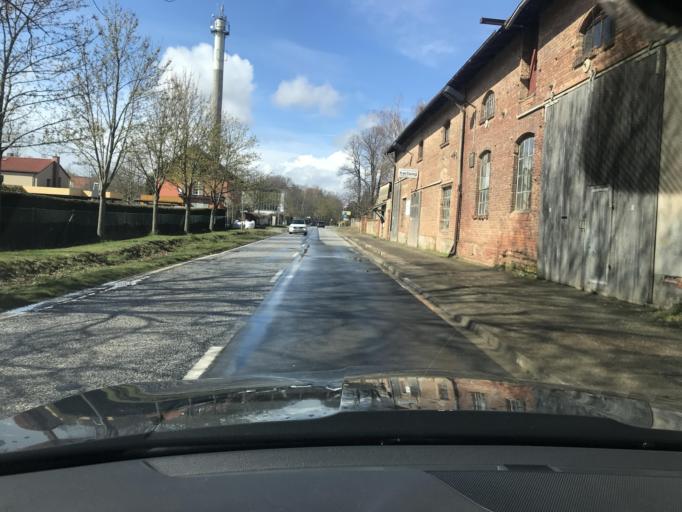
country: DE
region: Saxony-Anhalt
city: Hoym
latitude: 51.7832
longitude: 11.3218
